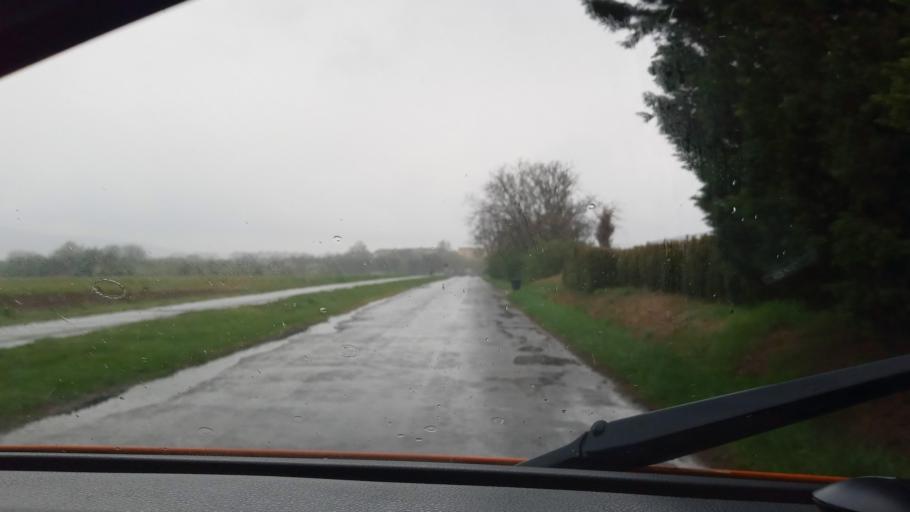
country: HU
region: Baranya
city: Pellerd
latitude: 46.0277
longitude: 18.2089
